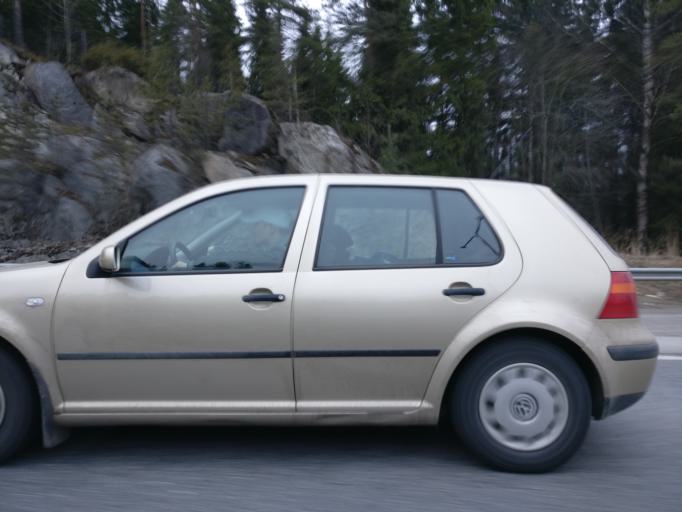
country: FI
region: Pirkanmaa
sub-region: Tampere
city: Tampere
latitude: 61.4644
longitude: 23.8098
